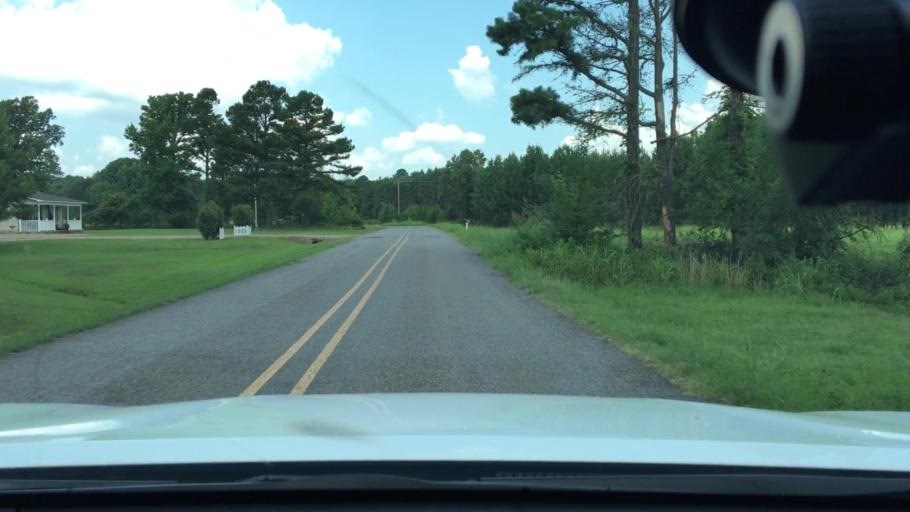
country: US
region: Arkansas
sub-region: Logan County
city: Paris
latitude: 35.2688
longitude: -93.6682
